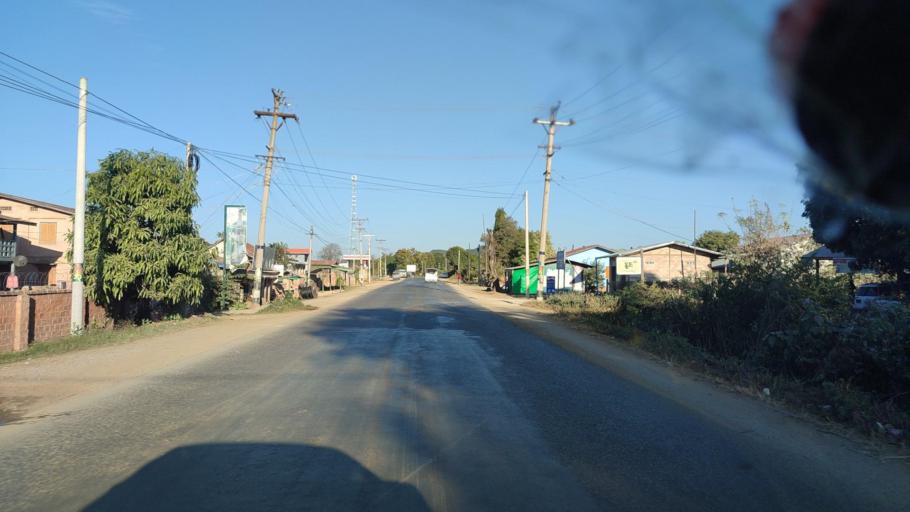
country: MM
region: Mandalay
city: Mogok
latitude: 22.5110
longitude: 97.0295
